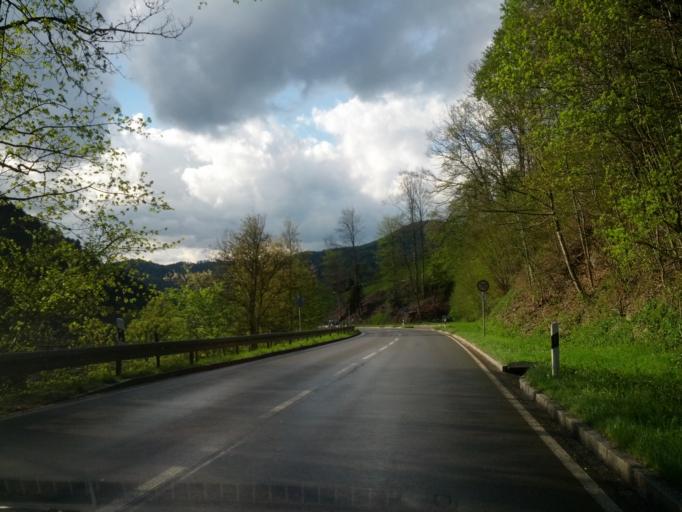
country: DE
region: Baden-Wuerttemberg
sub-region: Freiburg Region
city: Glottertal
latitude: 48.0335
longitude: 7.9929
